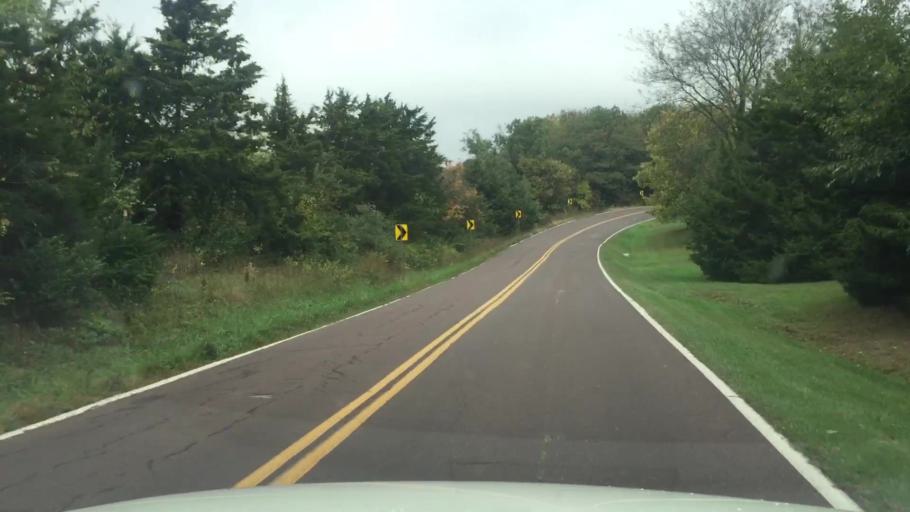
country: US
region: Missouri
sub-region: Boone County
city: Columbia
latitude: 38.8462
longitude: -92.3371
